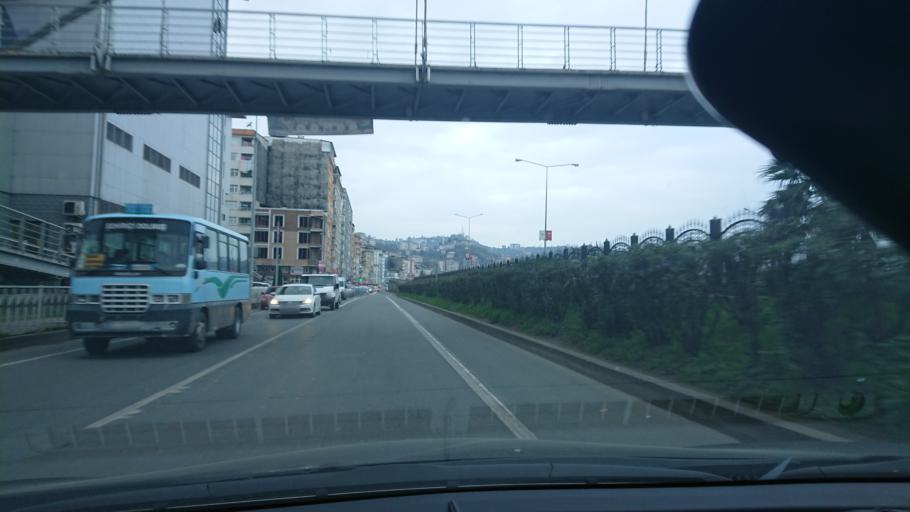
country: TR
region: Rize
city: Rize
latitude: 41.0256
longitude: 40.5257
